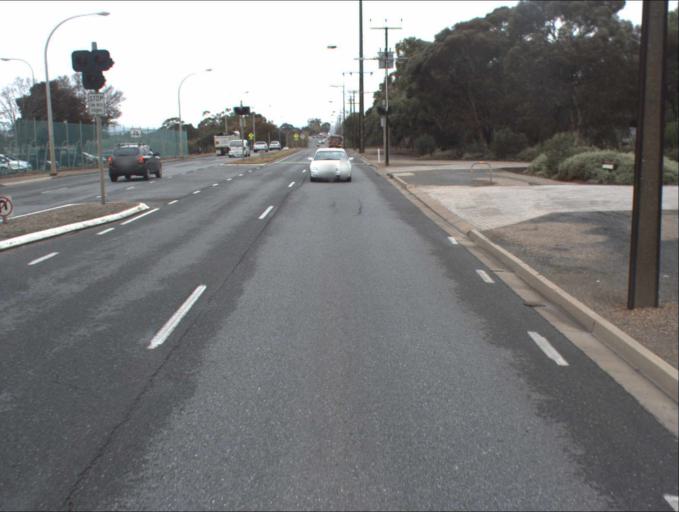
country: AU
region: South Australia
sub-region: Port Adelaide Enfield
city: Gilles Plains
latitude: -34.8466
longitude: 138.6418
